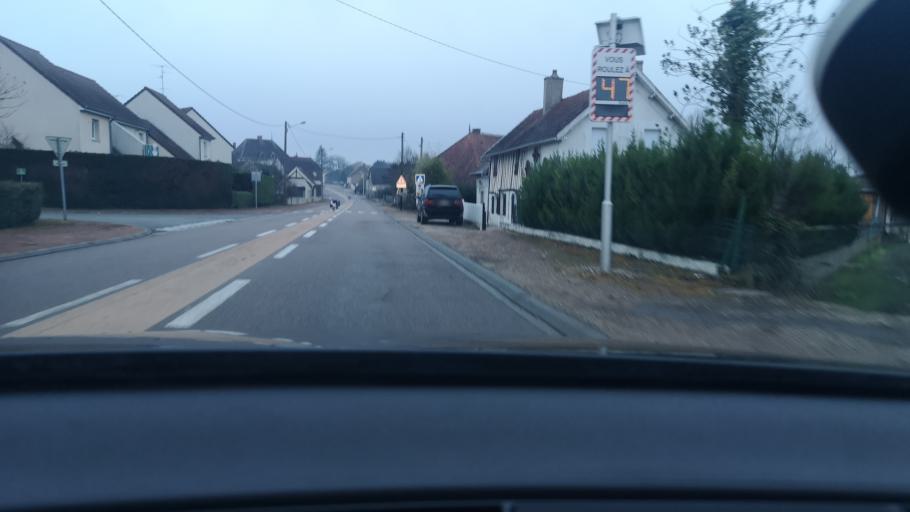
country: FR
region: Bourgogne
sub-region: Departement de la Cote-d'Or
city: Fenay
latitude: 47.1742
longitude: 5.0787
